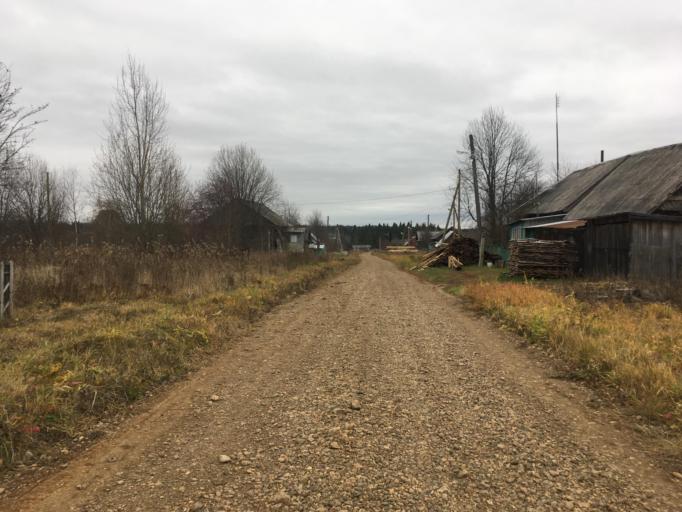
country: RU
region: Perm
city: Komarikhinskiy
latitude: 58.0914
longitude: 57.1115
